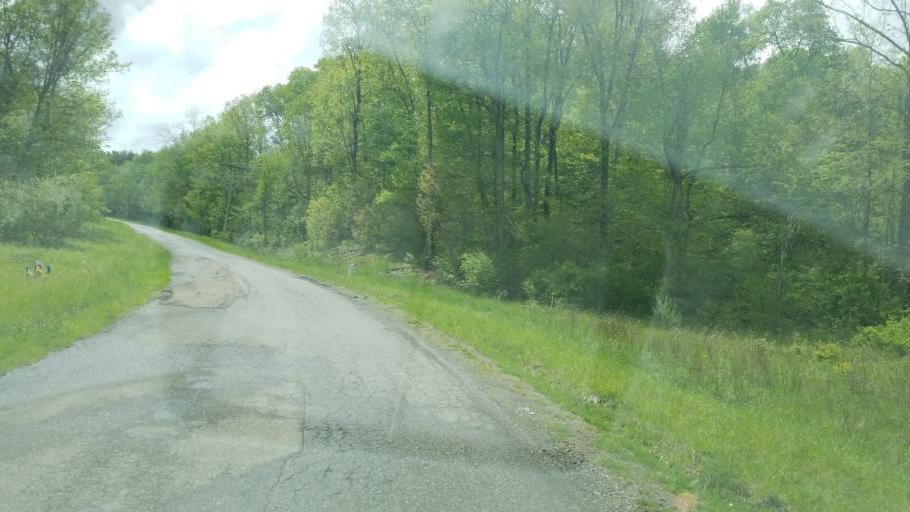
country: US
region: Ohio
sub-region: Tuscarawas County
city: Rockford
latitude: 40.4237
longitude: -81.2207
